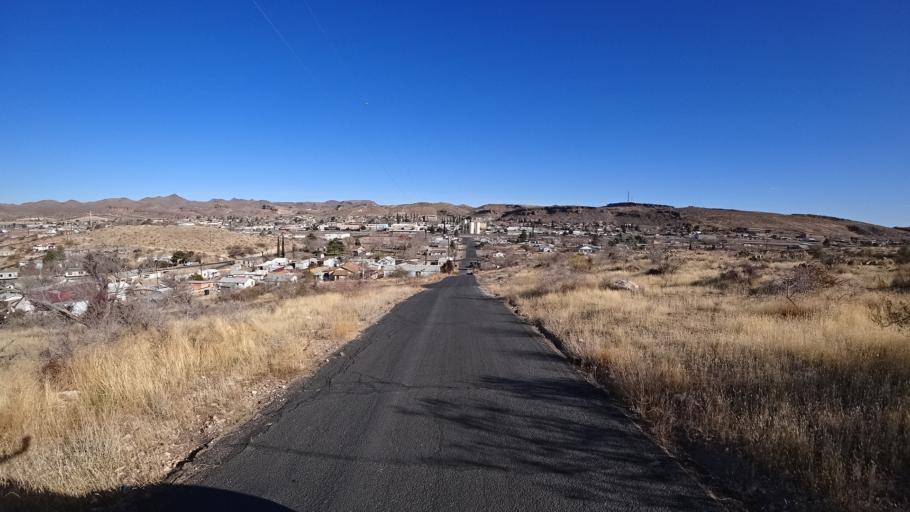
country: US
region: Arizona
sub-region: Mohave County
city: Kingman
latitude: 35.1832
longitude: -114.0523
